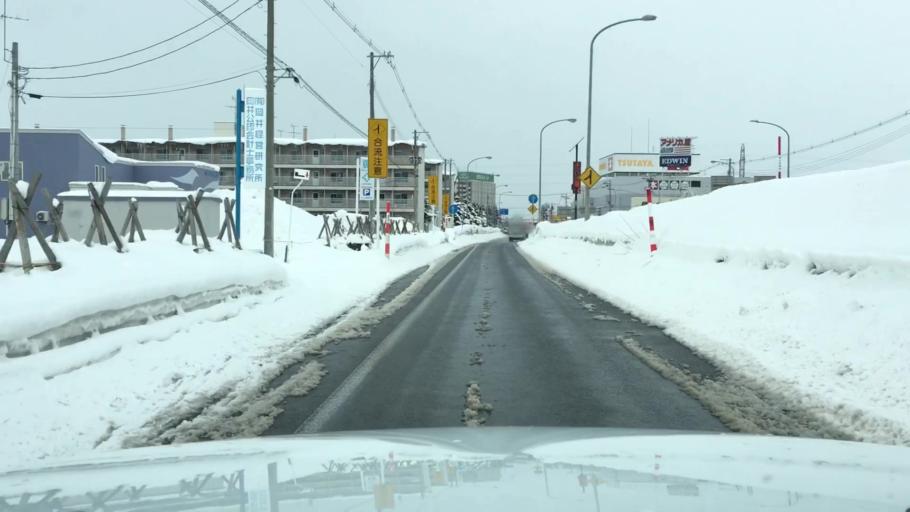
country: JP
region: Aomori
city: Hirosaki
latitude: 40.5984
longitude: 140.5019
